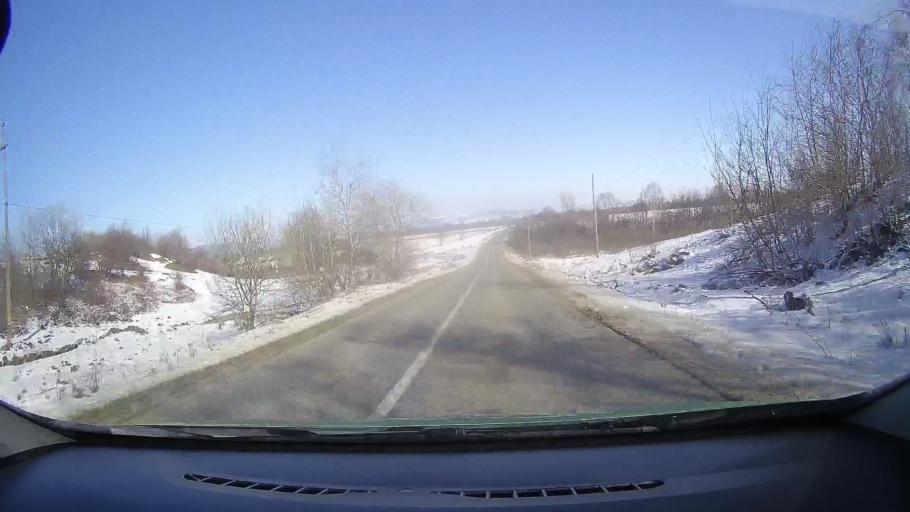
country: RO
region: Brasov
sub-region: Oras Victoria
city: Victoria
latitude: 45.7358
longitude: 24.7324
